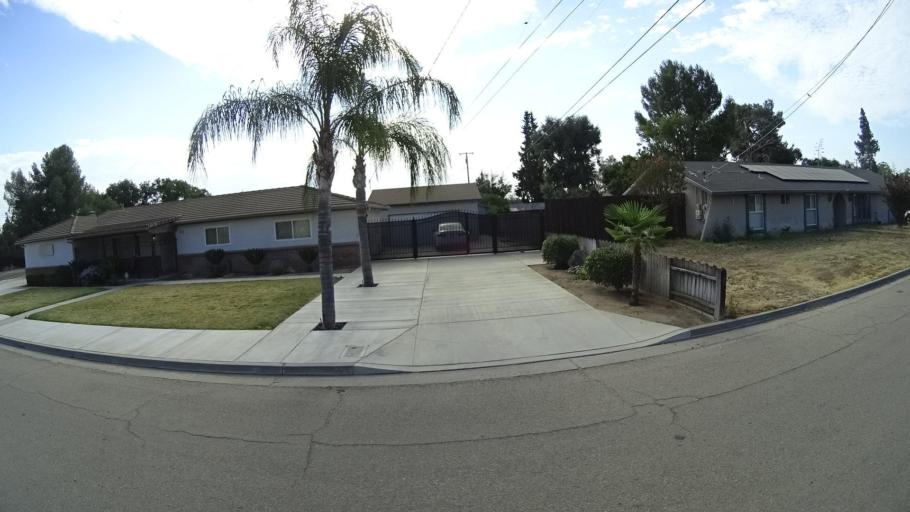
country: US
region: California
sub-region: Fresno County
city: Sunnyside
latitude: 36.7099
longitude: -119.6956
